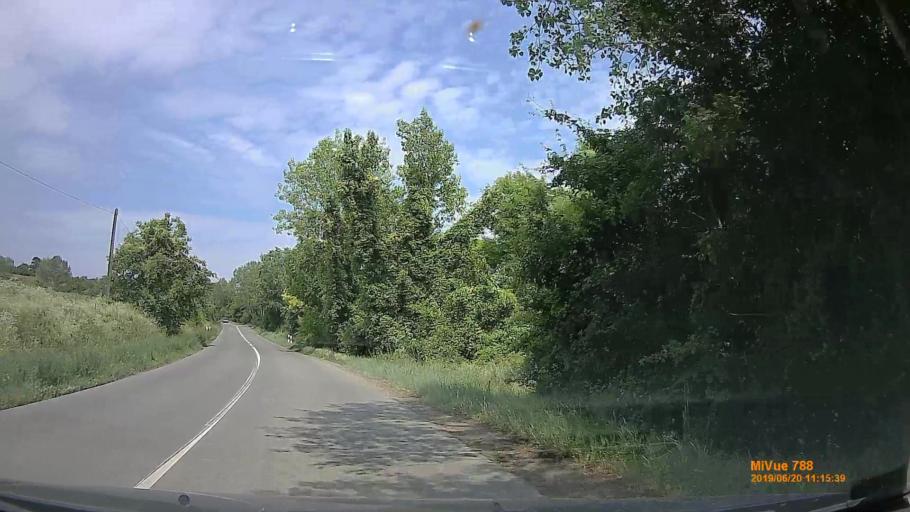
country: HU
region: Baranya
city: Pecsvarad
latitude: 46.1516
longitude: 18.4861
